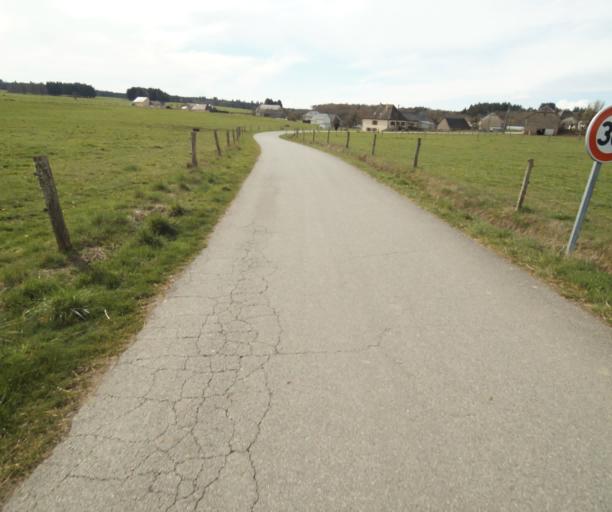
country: FR
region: Limousin
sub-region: Departement de la Correze
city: Correze
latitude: 45.3555
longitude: 1.8857
